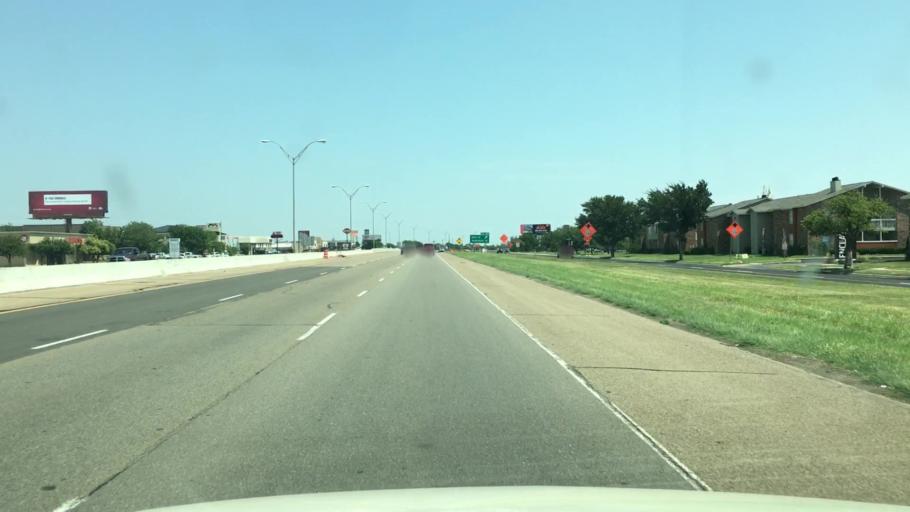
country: US
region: Texas
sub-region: Potter County
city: Amarillo
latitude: 35.1881
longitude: -101.9111
